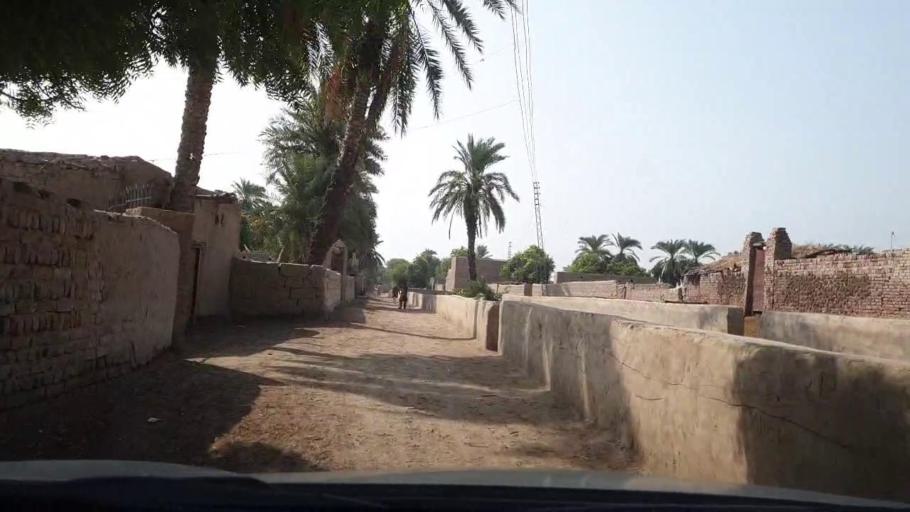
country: PK
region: Sindh
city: Larkana
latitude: 27.4643
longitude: 68.2441
